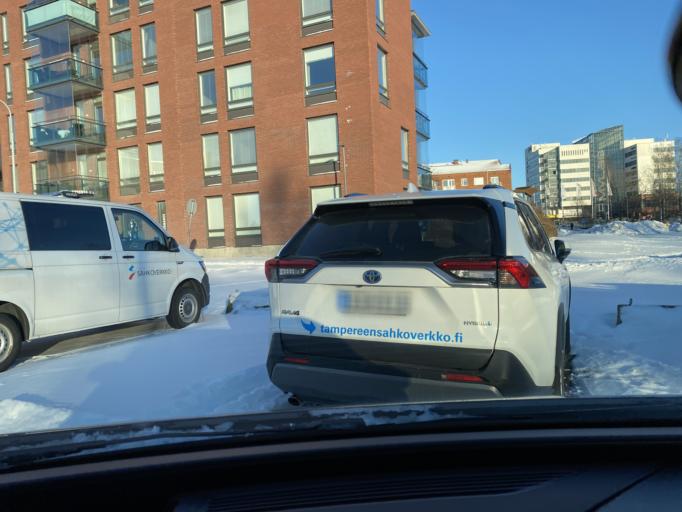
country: FI
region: Pirkanmaa
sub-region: Tampere
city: Tampere
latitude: 61.4905
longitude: 23.7683
